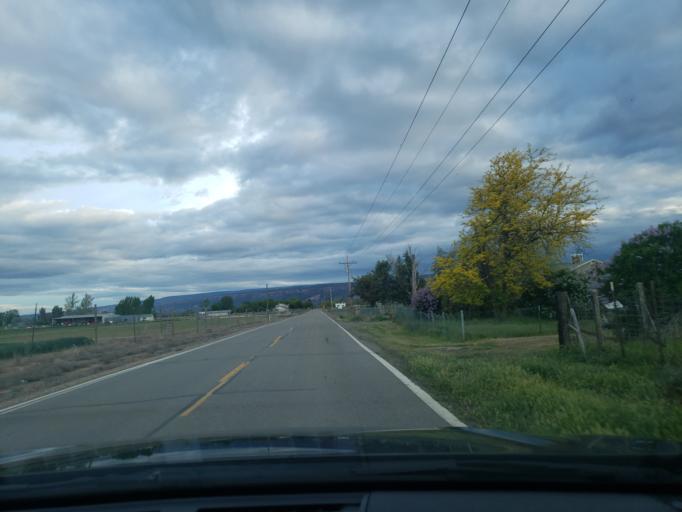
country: US
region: Colorado
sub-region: Mesa County
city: Fruita
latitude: 39.1830
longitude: -108.7013
